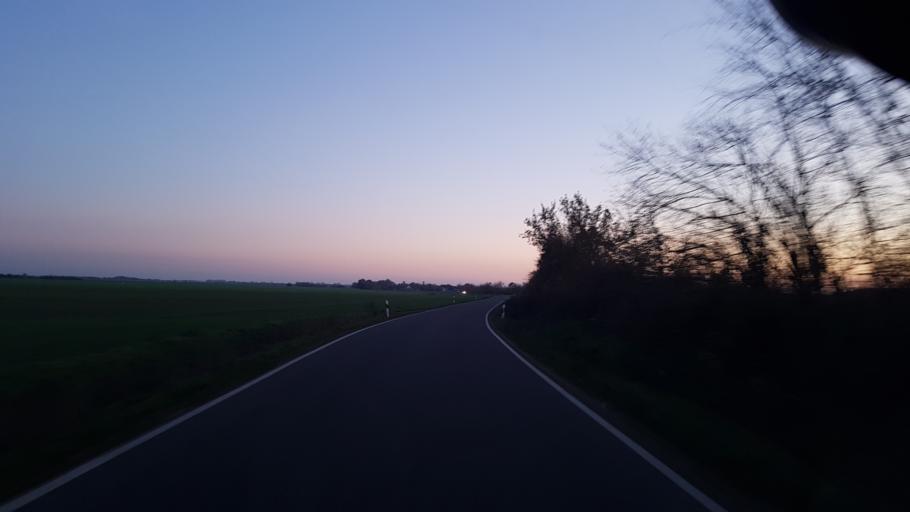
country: DE
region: Saxony
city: Arzberg
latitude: 51.5478
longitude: 13.1358
